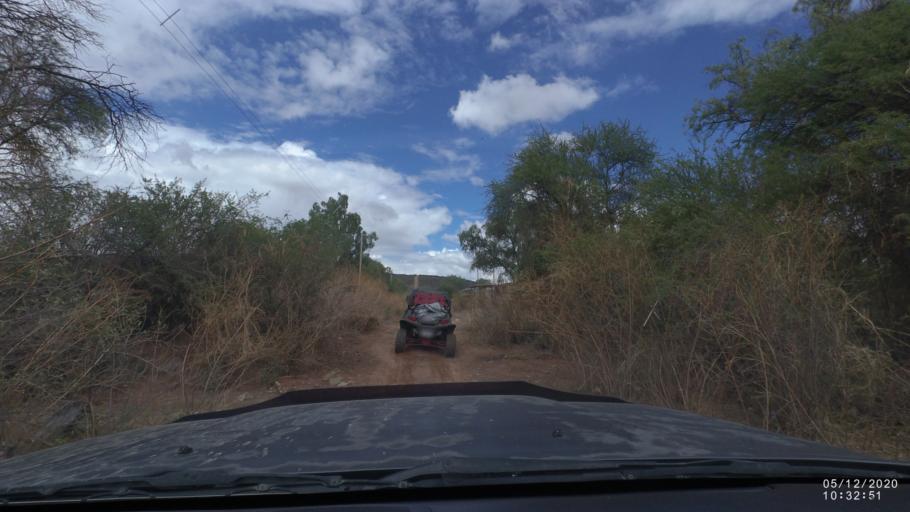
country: BO
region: Cochabamba
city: Sipe Sipe
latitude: -17.5458
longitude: -66.2705
